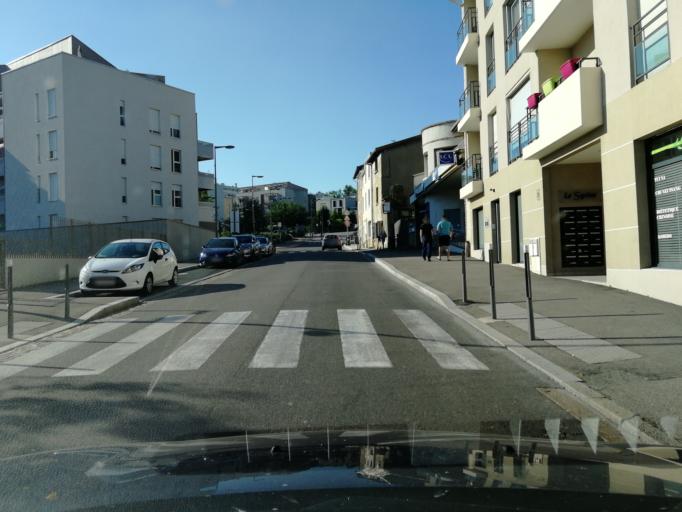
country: FR
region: Rhone-Alpes
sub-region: Departement du Rhone
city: Fontaines-sur-Saone
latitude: 45.8355
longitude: 4.8474
